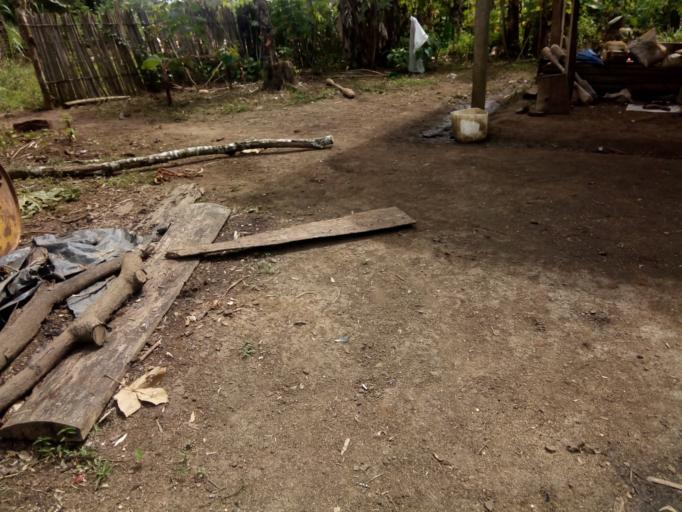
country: CR
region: Alajuela
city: San Jose
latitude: 11.0569
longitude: -85.1946
